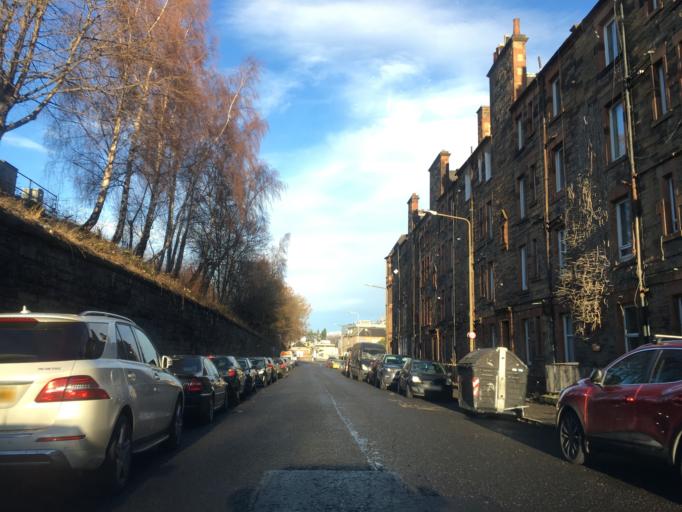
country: GB
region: Scotland
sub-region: Edinburgh
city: Colinton
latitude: 55.9375
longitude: -3.2369
